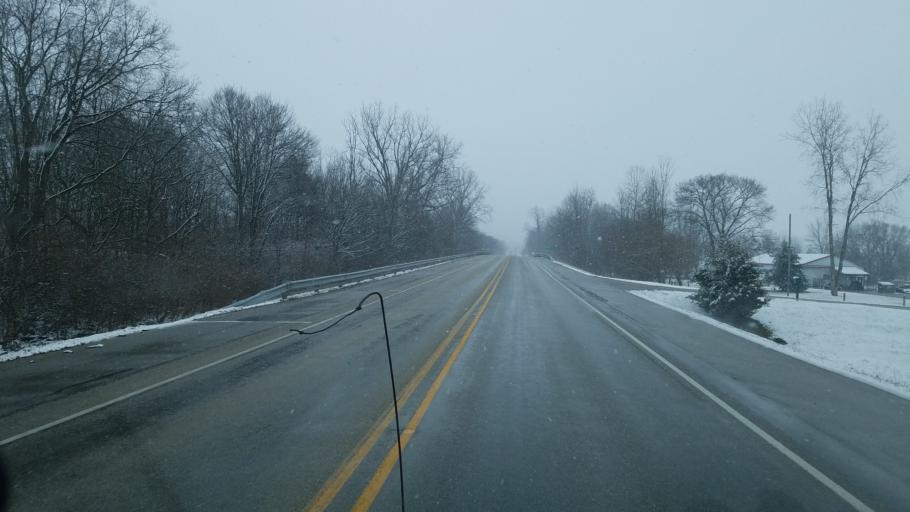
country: US
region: Indiana
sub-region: Wayne County
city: Centerville
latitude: 39.9071
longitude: -84.9524
